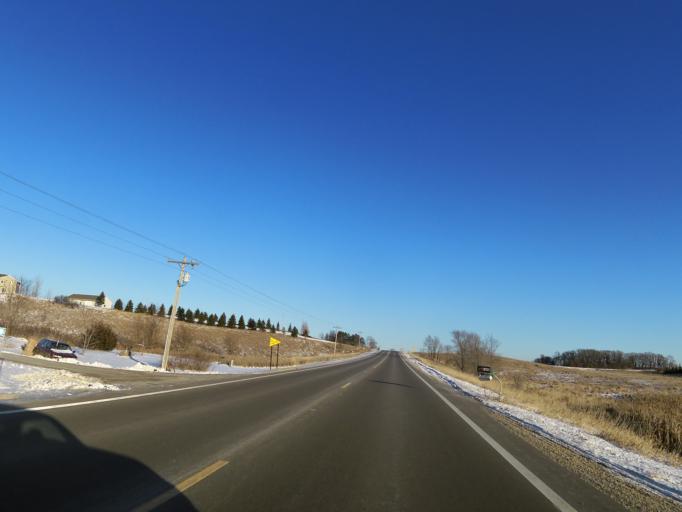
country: US
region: Minnesota
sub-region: Scott County
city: Elko New Market
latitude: 44.5440
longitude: -93.3315
